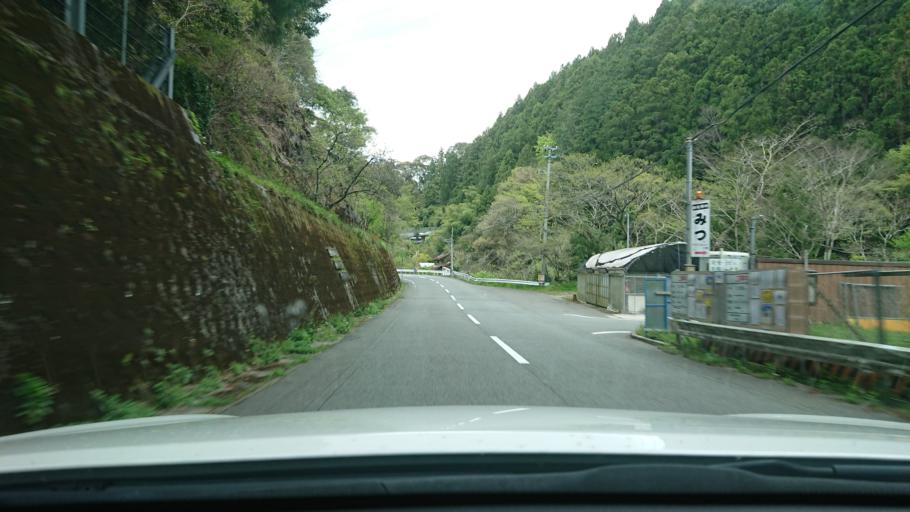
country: JP
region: Tokushima
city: Ishii
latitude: 33.9138
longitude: 134.4209
